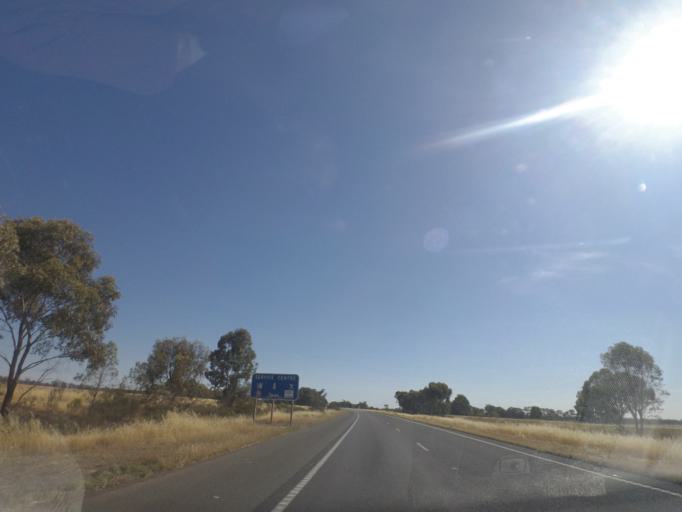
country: AU
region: Victoria
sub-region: Greater Shepparton
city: Shepparton
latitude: -36.6998
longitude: 145.2068
